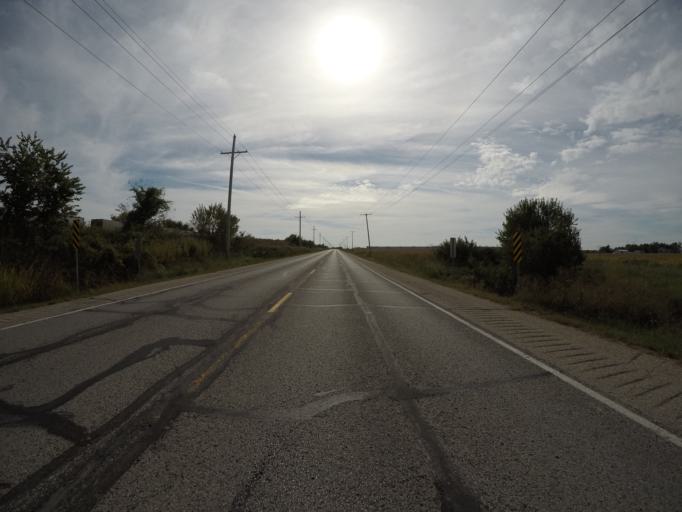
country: US
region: Kansas
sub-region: Johnson County
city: Gardner
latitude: 38.8245
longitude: -94.8754
